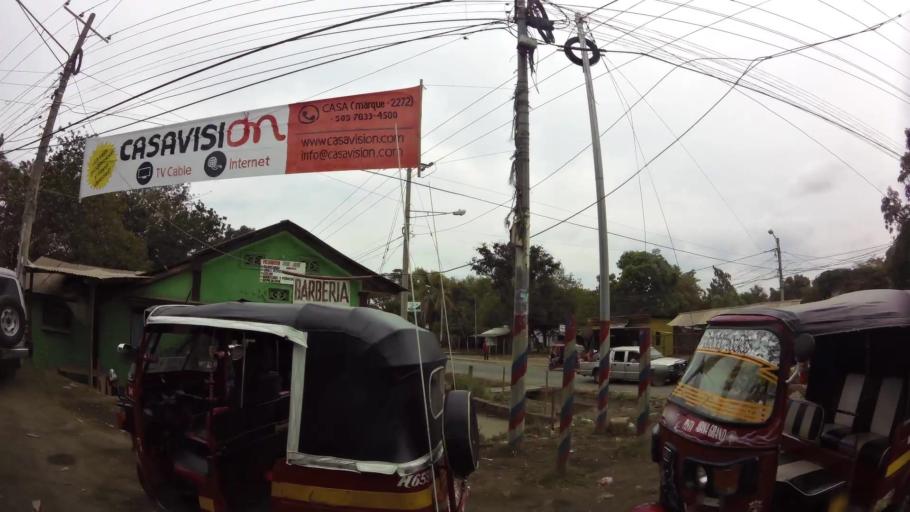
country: NI
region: Managua
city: Managua
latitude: 12.1250
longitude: -86.1736
